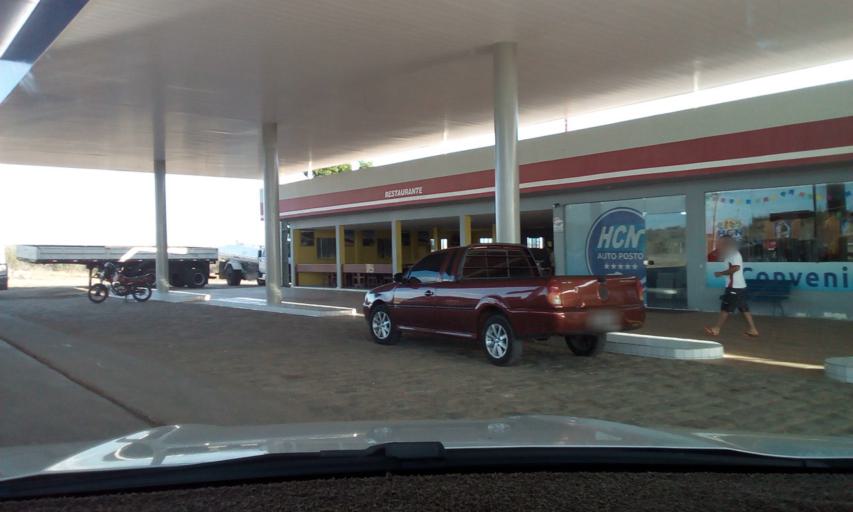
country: BR
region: Paraiba
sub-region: Pocinhos
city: Pocinhos
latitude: -7.1536
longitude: -36.1025
